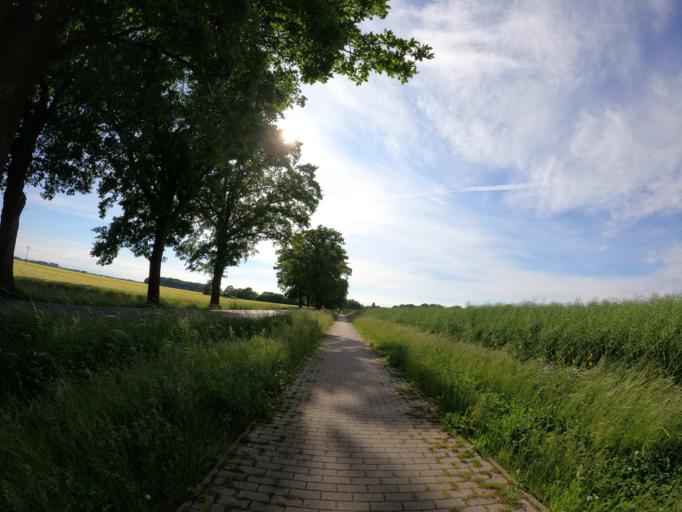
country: DE
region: Mecklenburg-Vorpommern
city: Preetz
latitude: 54.3492
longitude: 12.9978
